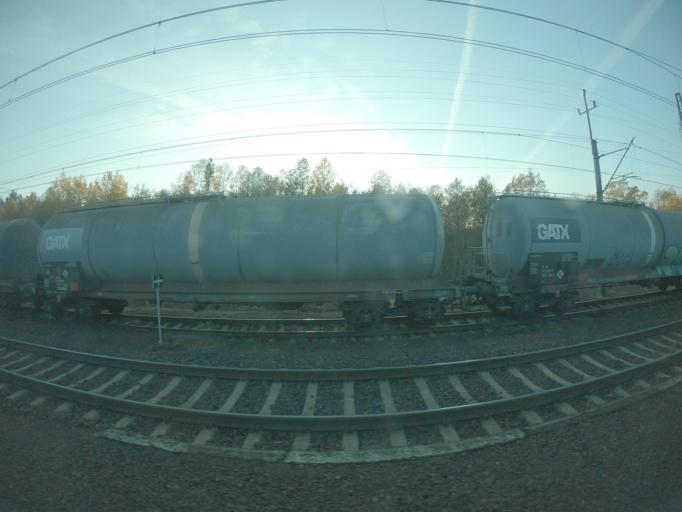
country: PL
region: Lubusz
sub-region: Powiat slubicki
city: Rzepin
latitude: 52.3058
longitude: 14.8685
